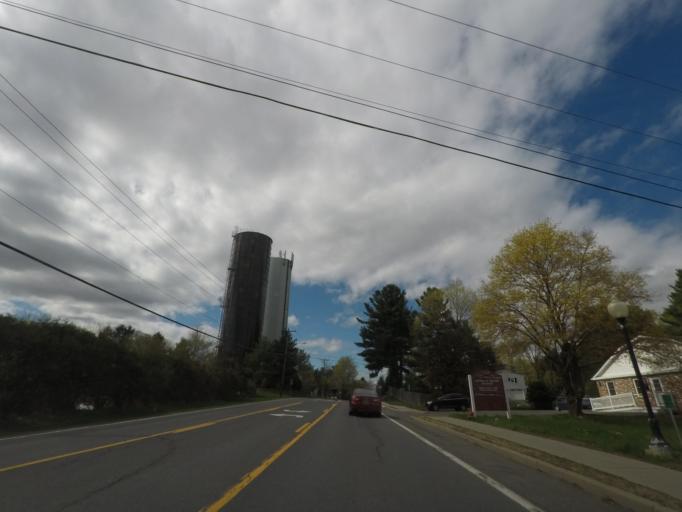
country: US
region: New York
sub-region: Columbia County
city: Valatie
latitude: 42.4160
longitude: -73.6827
